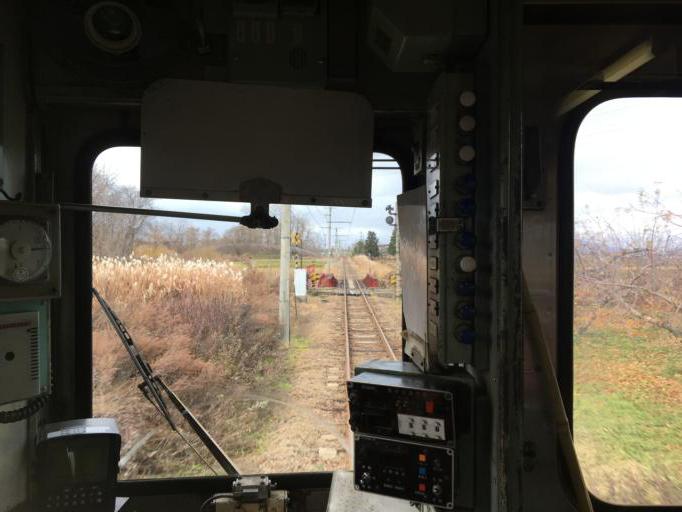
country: JP
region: Aomori
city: Hirosaki
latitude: 40.5609
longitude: 140.4962
